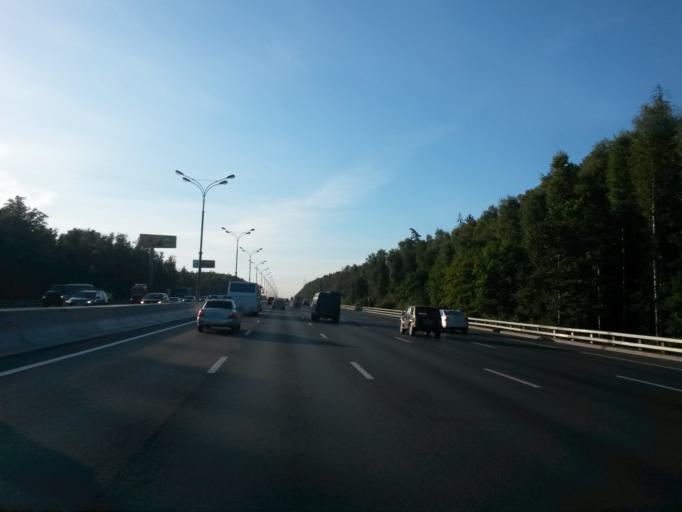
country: RU
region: Moscow
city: Gol'yanovo
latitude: 55.8436
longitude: 37.8014
